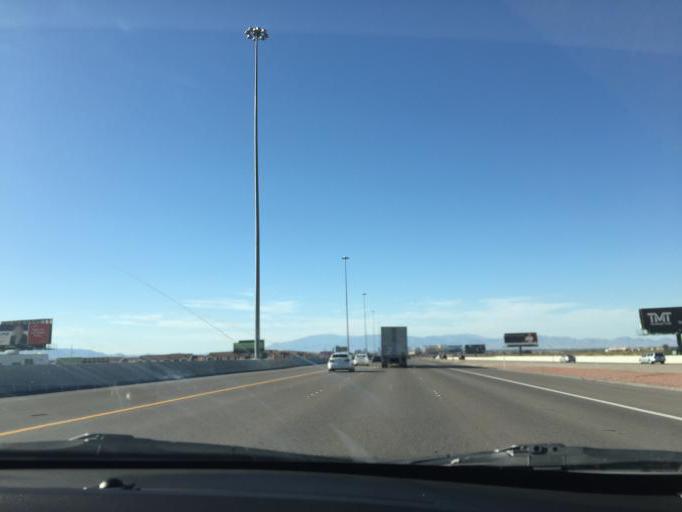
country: US
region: Nevada
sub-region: Clark County
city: Enterprise
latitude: 35.9660
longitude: -115.1815
